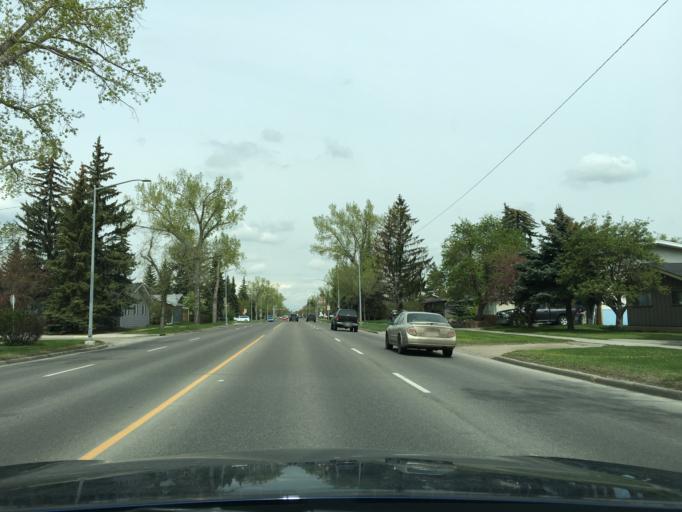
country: CA
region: Alberta
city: Calgary
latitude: 50.9826
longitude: -114.0831
